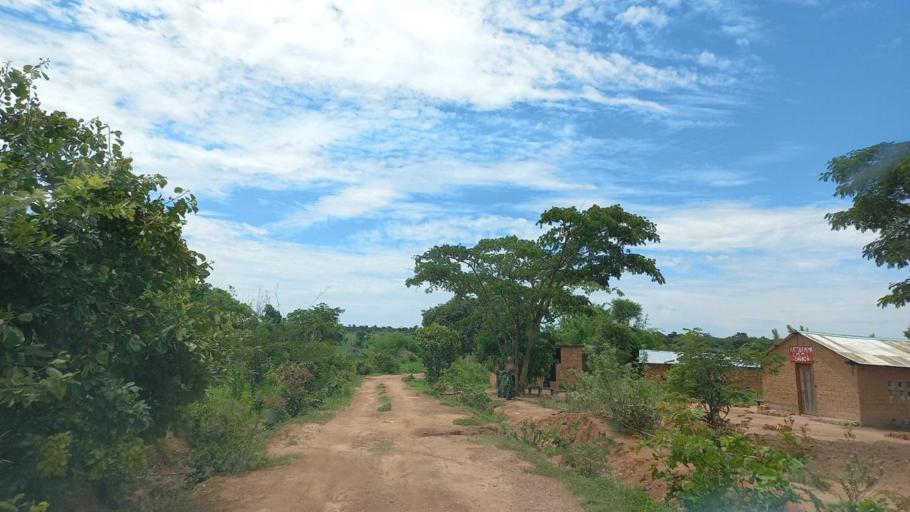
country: ZM
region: Copperbelt
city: Kitwe
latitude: -12.8159
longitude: 28.3902
